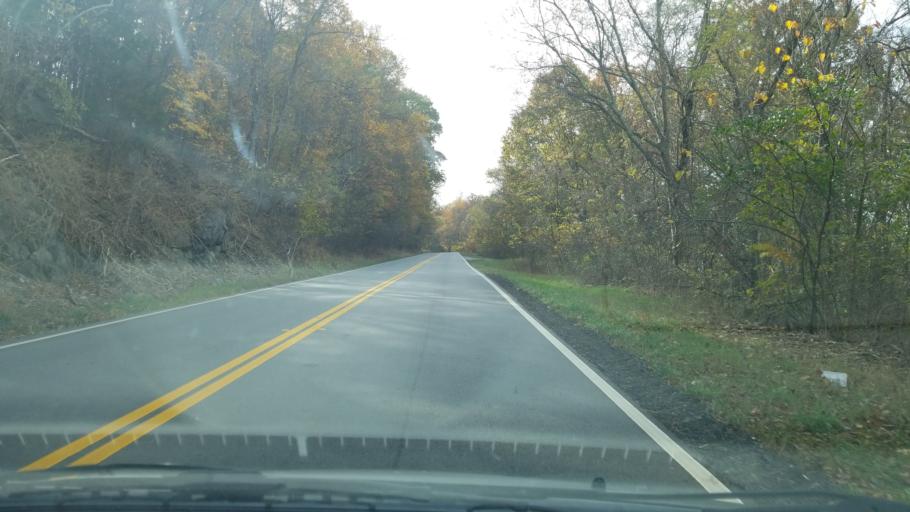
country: US
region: Georgia
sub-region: Dade County
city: Trenton
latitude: 34.8452
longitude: -85.4970
